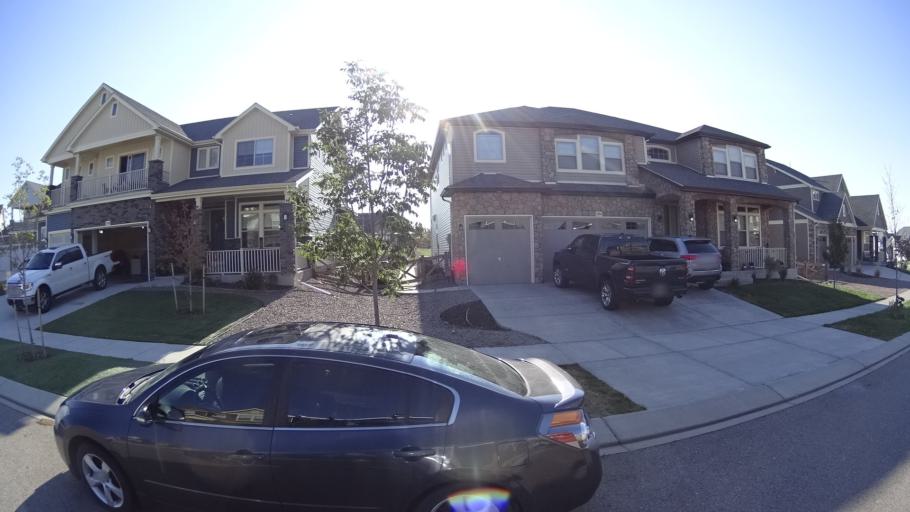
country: US
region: Colorado
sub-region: El Paso County
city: Black Forest
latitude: 38.9365
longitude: -104.6705
